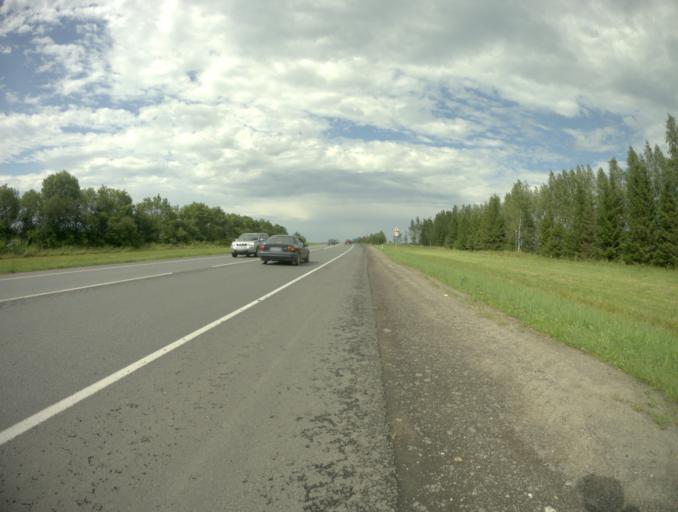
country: RU
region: Vladimir
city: Suzdal'
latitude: 56.3400
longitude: 40.4747
